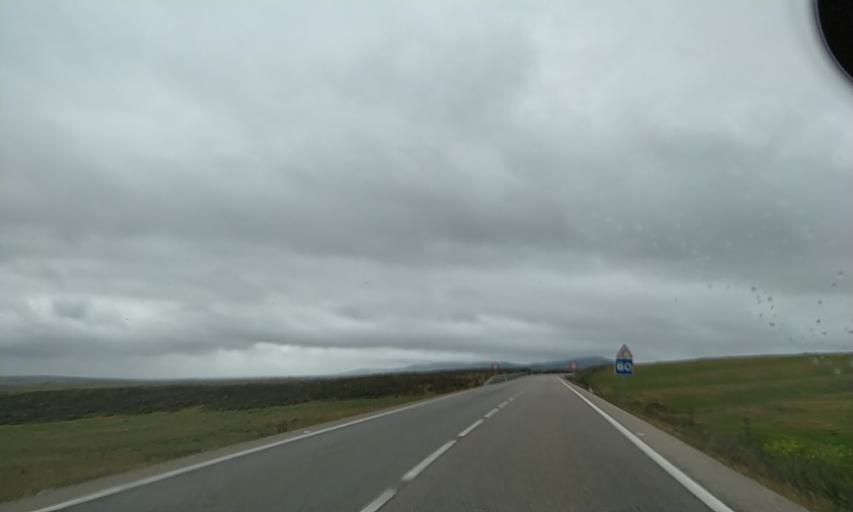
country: ES
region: Extremadura
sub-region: Provincia de Caceres
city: Casar de Caceres
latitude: 39.5270
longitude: -6.4004
